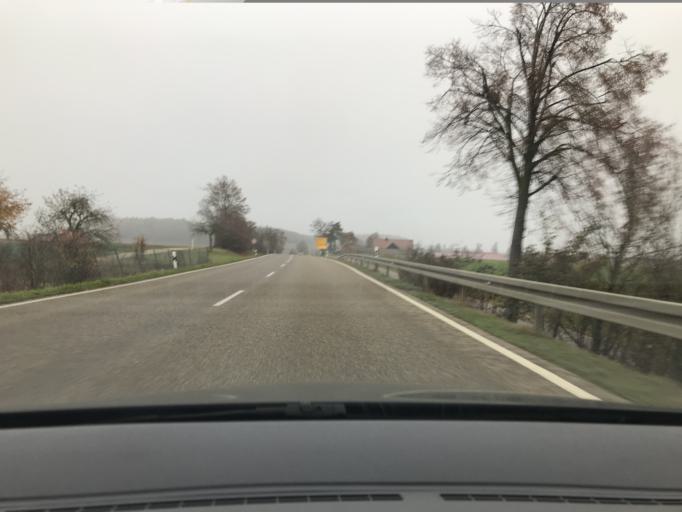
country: DE
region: Bavaria
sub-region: Swabia
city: Marktoffingen
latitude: 48.9400
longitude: 10.4608
